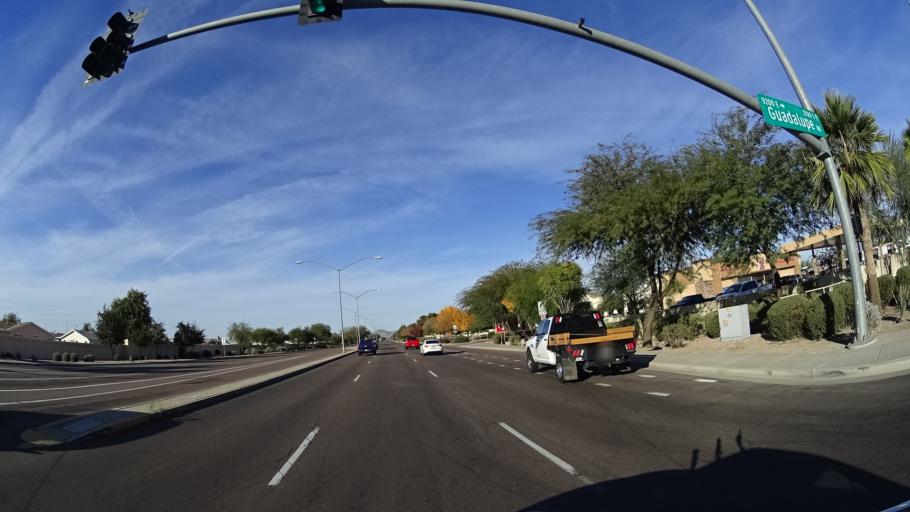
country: US
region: Arizona
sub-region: Pinal County
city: Apache Junction
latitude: 33.3647
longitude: -111.6359
